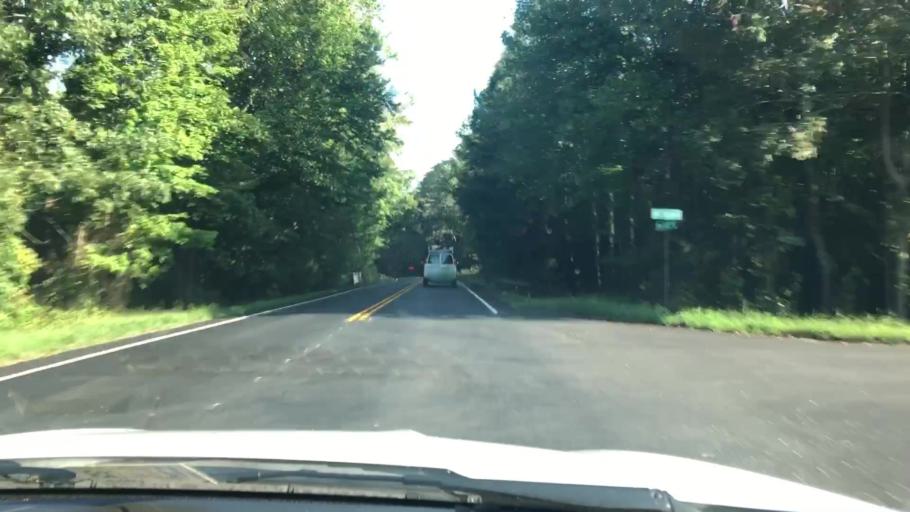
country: US
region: Virginia
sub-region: King William County
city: West Point
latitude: 37.4760
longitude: -76.8463
